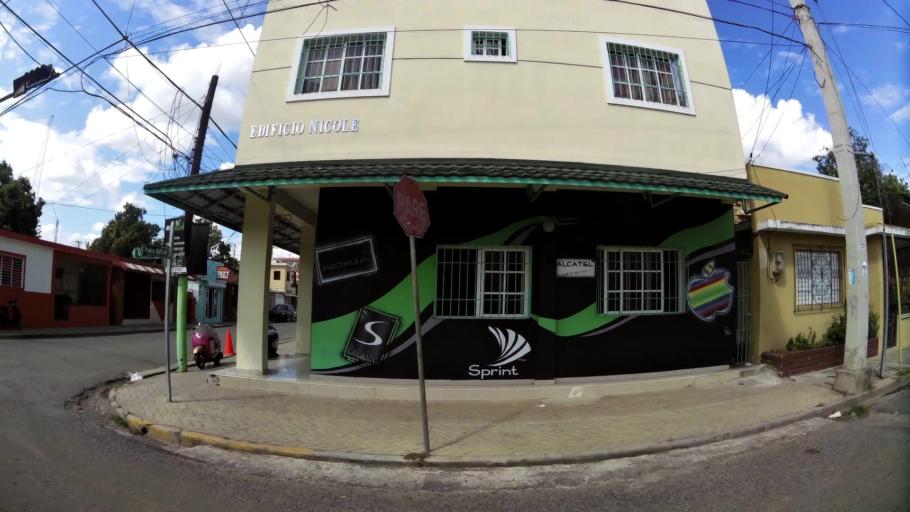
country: DO
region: La Vega
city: Concepcion de La Vega
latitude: 19.2233
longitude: -70.5340
